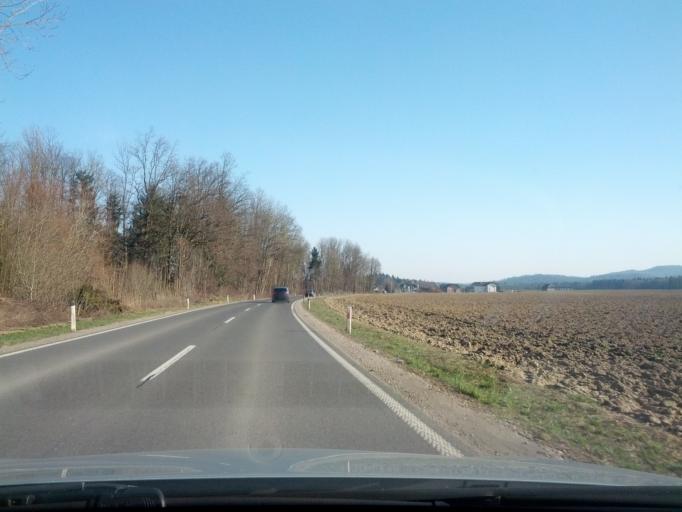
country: SI
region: Cerklje na Gorenjskem
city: Cerklje na Gorenjskem
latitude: 46.2230
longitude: 14.4968
